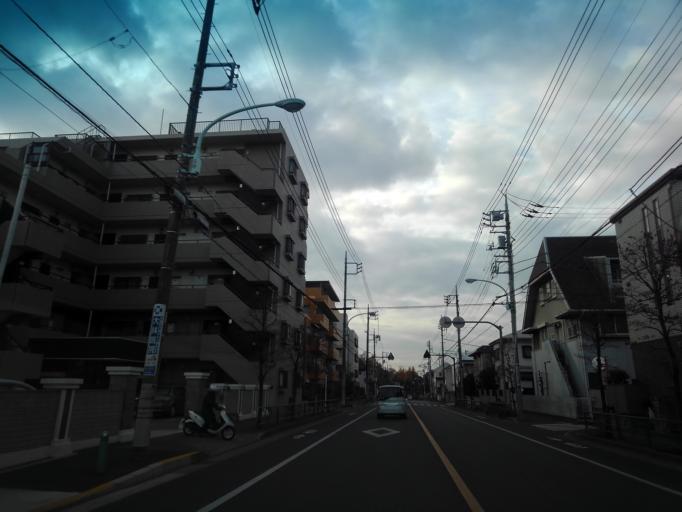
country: JP
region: Tokyo
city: Tanashicho
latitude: 35.7201
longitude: 139.5093
